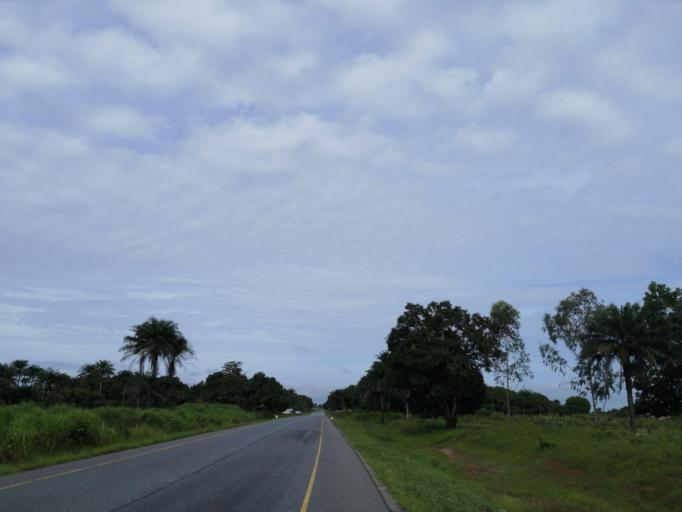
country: SL
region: Northern Province
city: Port Loko
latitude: 8.7729
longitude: -12.8665
